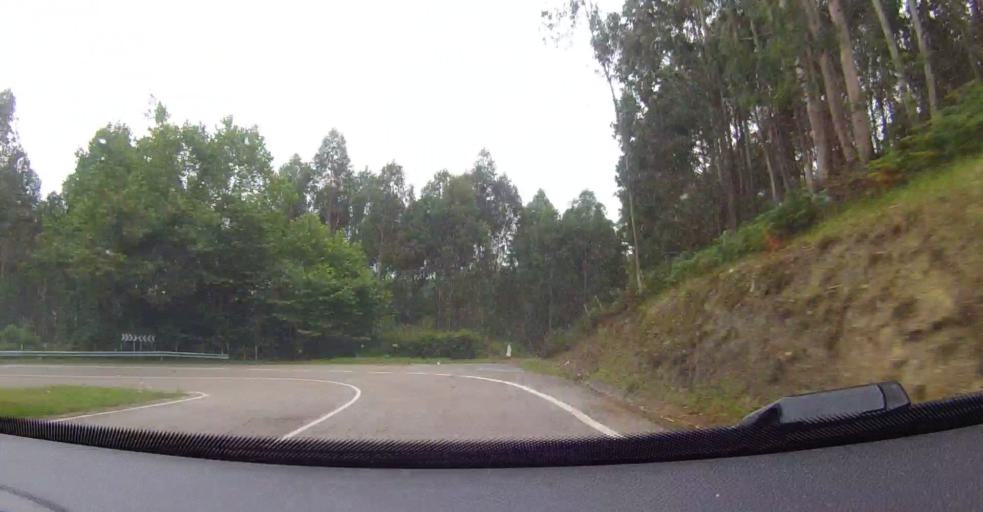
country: ES
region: Basque Country
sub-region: Bizkaia
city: Balmaseda
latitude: 43.2350
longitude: -3.2922
